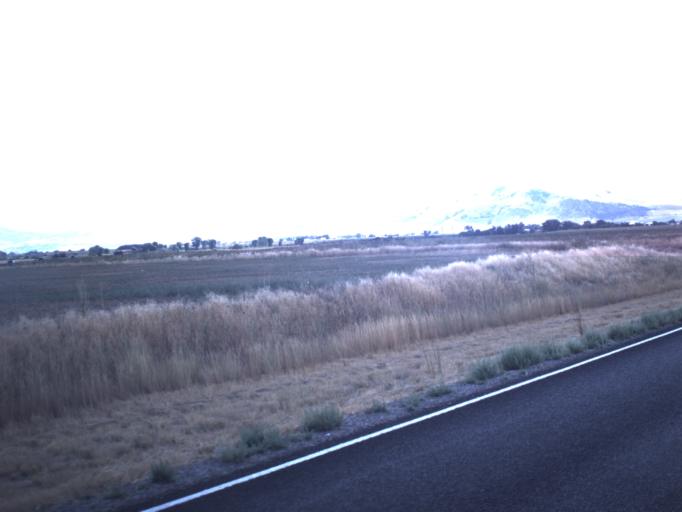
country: US
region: Utah
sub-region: Cache County
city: Lewiston
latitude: 41.9249
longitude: -111.8843
